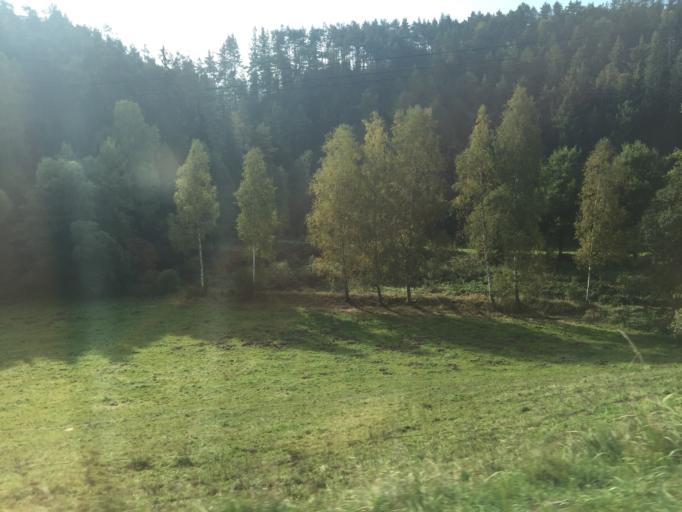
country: CZ
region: Ustecky
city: Benesov nad Ploucnici
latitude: 50.8115
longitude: 14.3379
